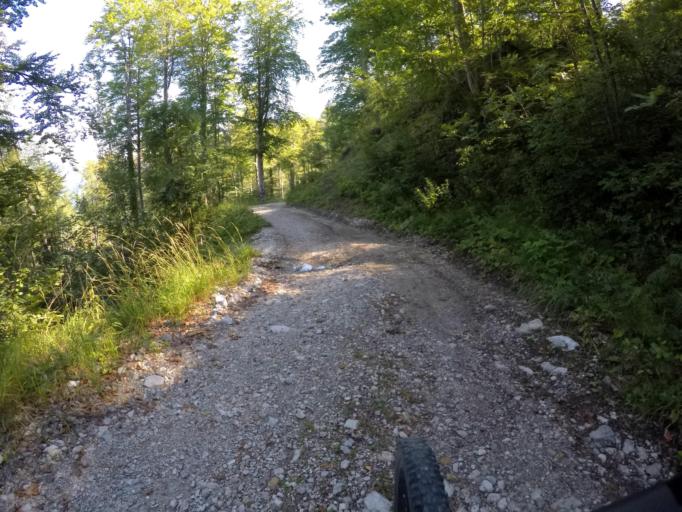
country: IT
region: Friuli Venezia Giulia
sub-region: Provincia di Udine
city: Zuglio
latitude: 46.4566
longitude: 13.0980
